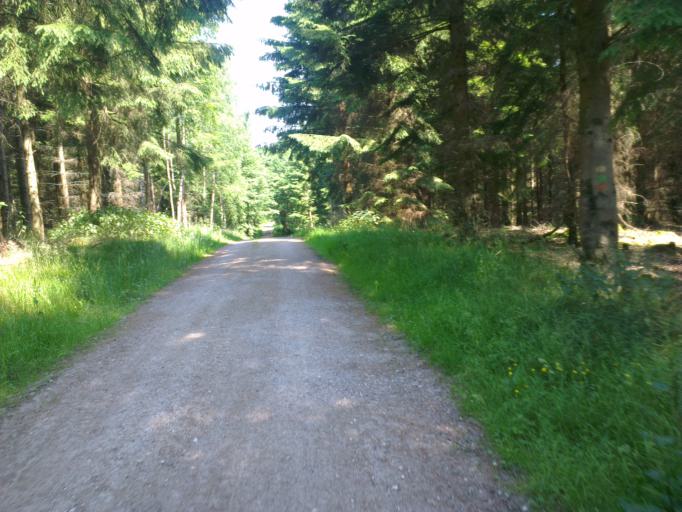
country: DK
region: Capital Region
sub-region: Allerod Kommune
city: Lillerod
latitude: 55.9237
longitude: 12.3614
